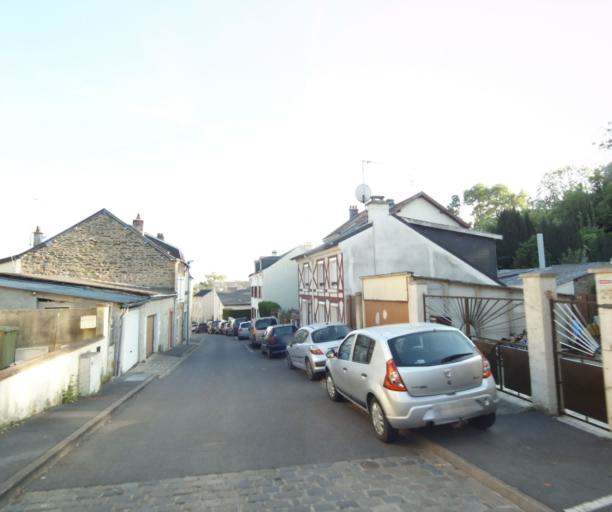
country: FR
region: Champagne-Ardenne
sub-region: Departement des Ardennes
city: Charleville-Mezieres
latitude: 49.7843
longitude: 4.7145
